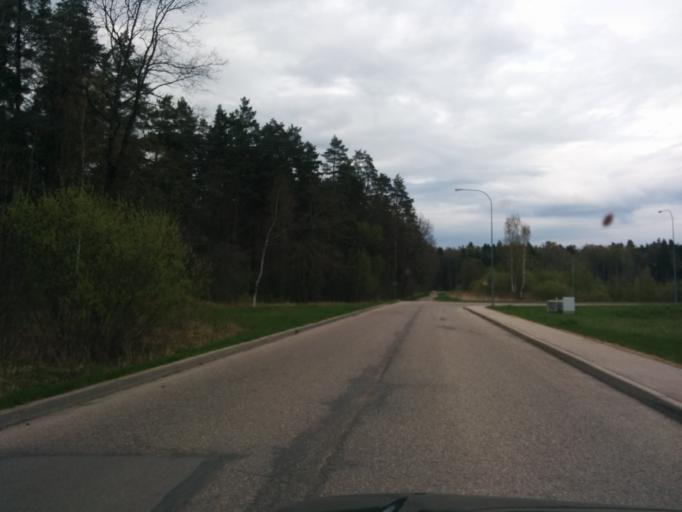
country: LV
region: Ozolnieku
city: Ozolnieki
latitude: 56.6681
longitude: 23.7728
